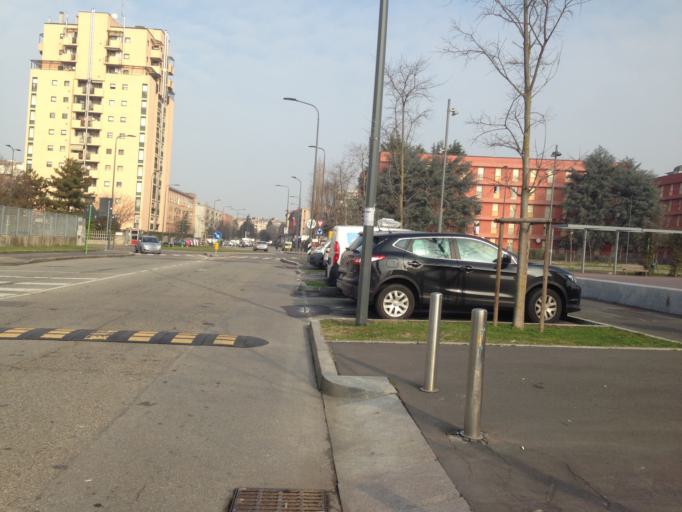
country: IT
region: Lombardy
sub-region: Citta metropolitana di Milano
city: Cesano Boscone
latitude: 45.4690
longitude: 9.1099
